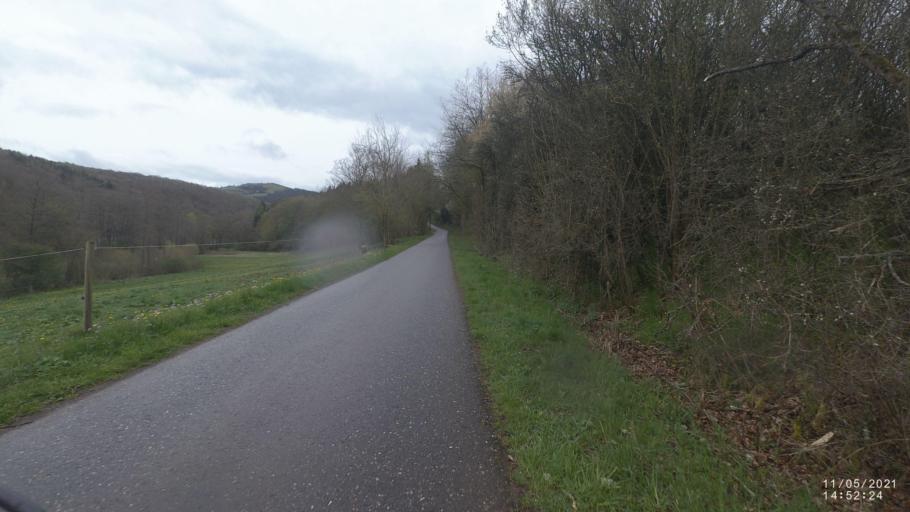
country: DE
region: Rheinland-Pfalz
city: Ditscheid
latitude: 50.2967
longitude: 7.0781
